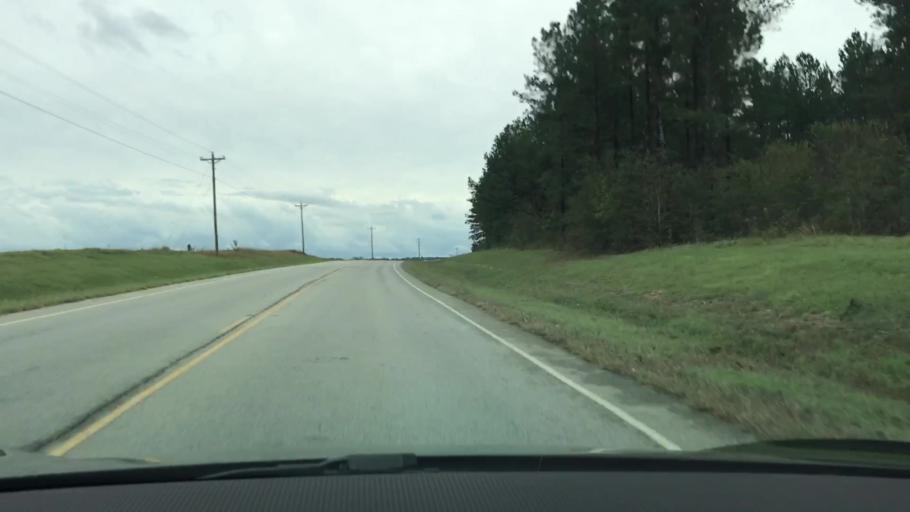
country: US
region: Georgia
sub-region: Jefferson County
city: Wrens
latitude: 33.1136
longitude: -82.4321
